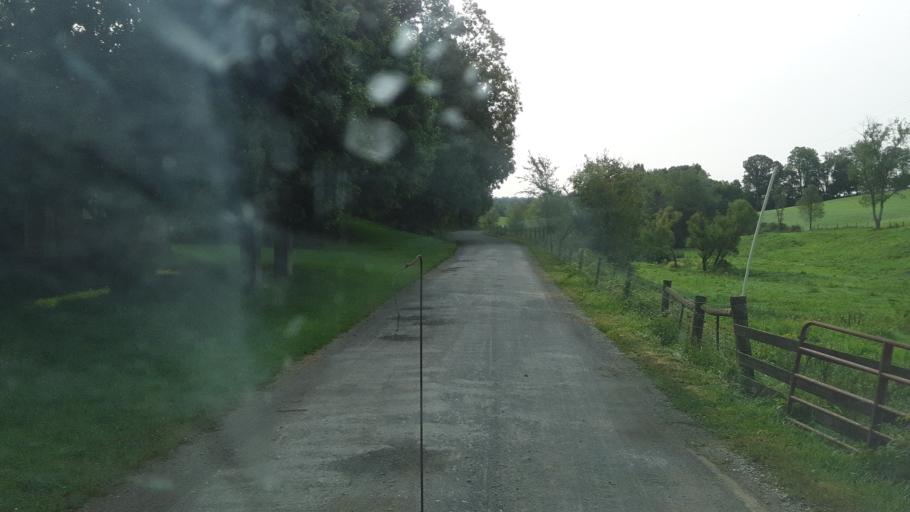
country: US
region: Ohio
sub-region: Holmes County
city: Millersburg
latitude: 40.4338
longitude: -81.8285
